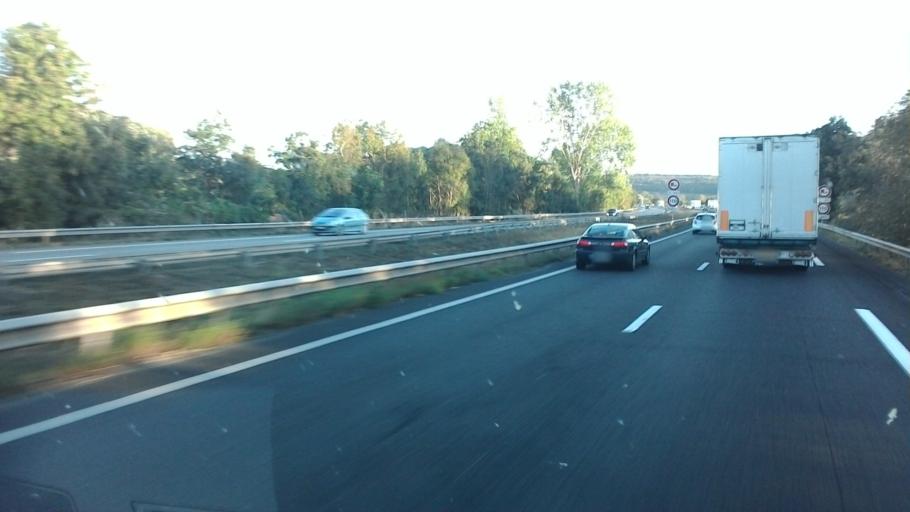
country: FR
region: Lorraine
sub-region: Departement de Meurthe-et-Moselle
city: Belleville
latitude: 48.8358
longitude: 6.0914
